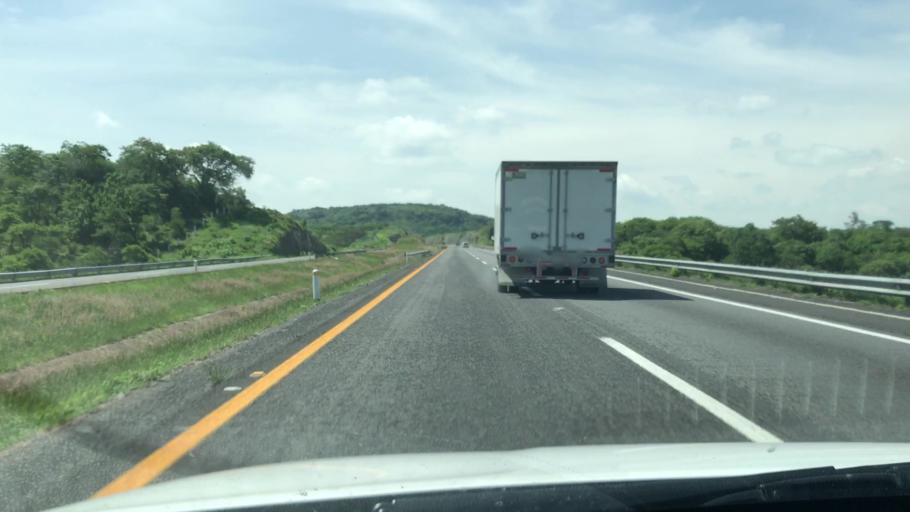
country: MX
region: Jalisco
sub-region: Zapotlan del Rey
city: Zapotlan del Rey
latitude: 20.4822
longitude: -102.9383
